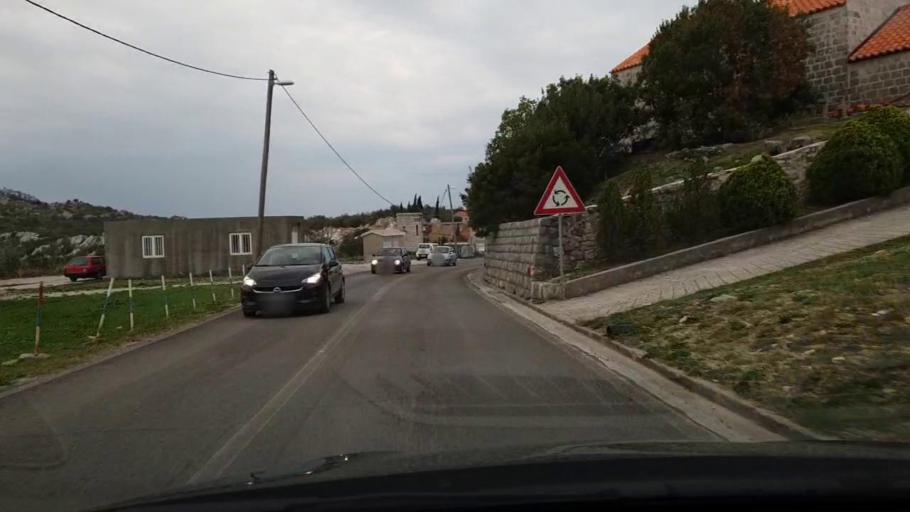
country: HR
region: Dubrovacko-Neretvanska
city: Cibaca
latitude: 42.6459
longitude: 18.1586
